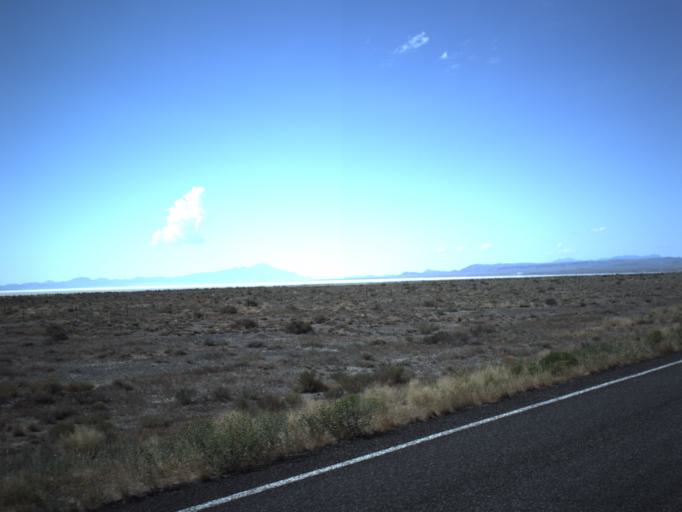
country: US
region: Utah
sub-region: Millard County
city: Delta
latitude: 39.1042
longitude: -113.1481
